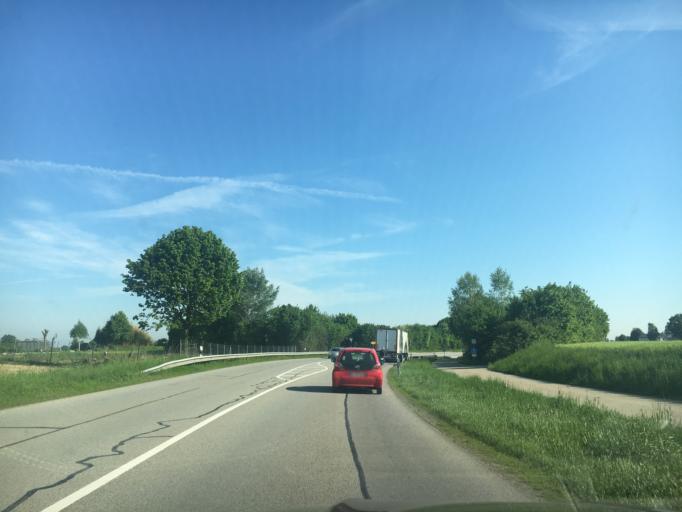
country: DE
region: Bavaria
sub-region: Upper Bavaria
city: Unterneukirchen
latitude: 48.1774
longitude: 12.6308
